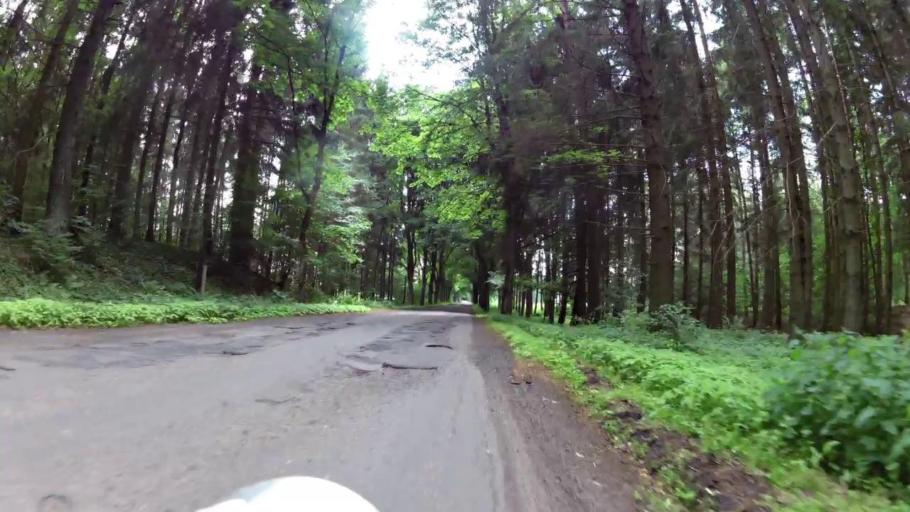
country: PL
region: West Pomeranian Voivodeship
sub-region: Powiat koszalinski
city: Bobolice
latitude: 53.9645
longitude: 16.7186
